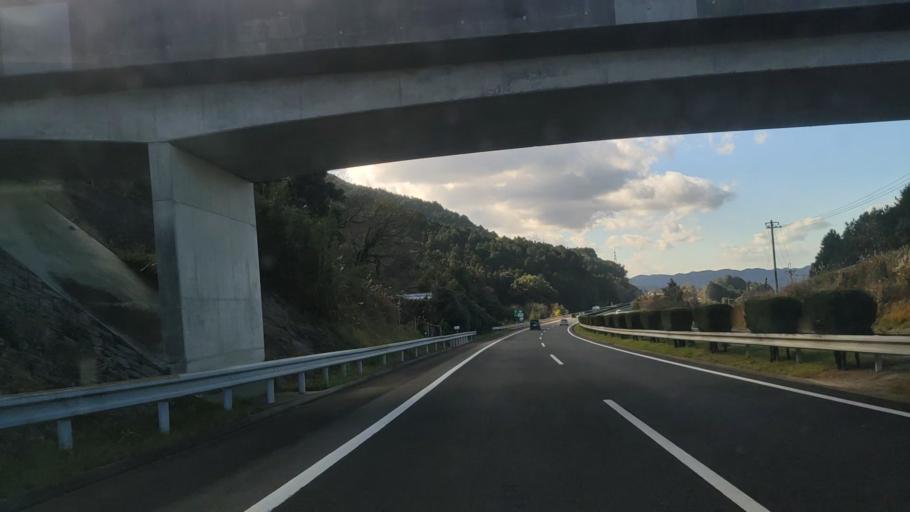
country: JP
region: Ehime
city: Niihama
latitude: 33.9511
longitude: 133.4374
